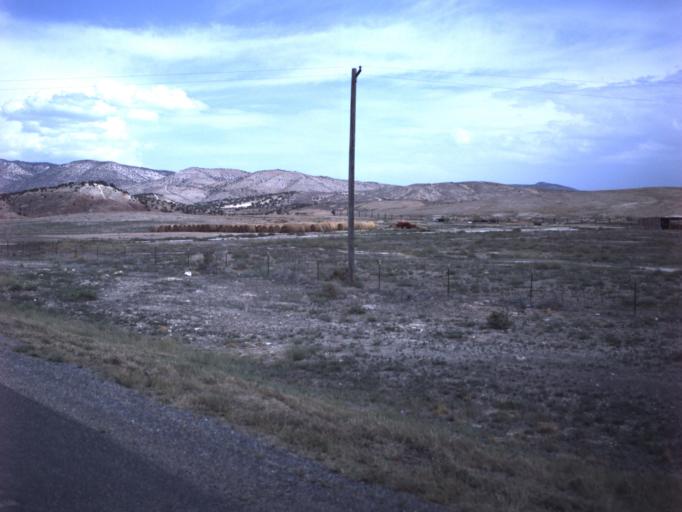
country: US
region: Utah
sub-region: Sanpete County
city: Gunnison
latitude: 39.2103
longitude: -111.8485
